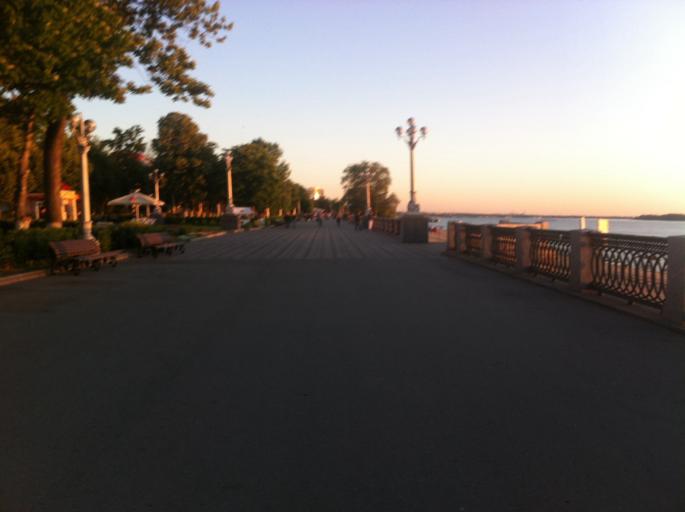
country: RU
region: Samara
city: Rozhdestveno
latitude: 53.1941
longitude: 50.0876
